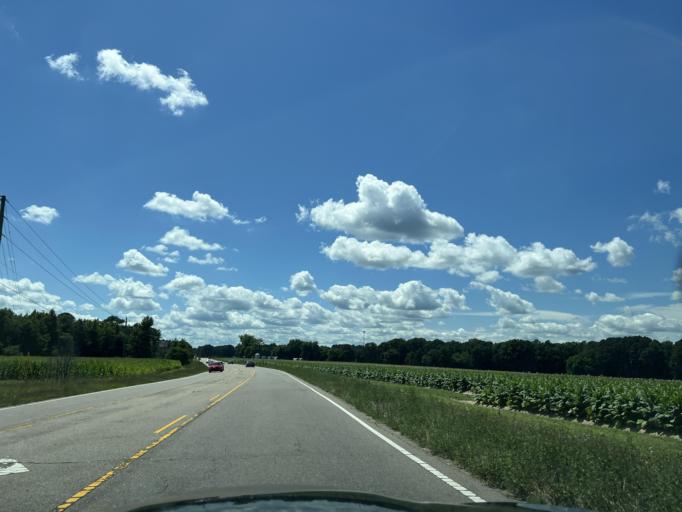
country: US
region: North Carolina
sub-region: Lee County
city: Sanford
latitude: 35.4373
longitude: -79.1947
